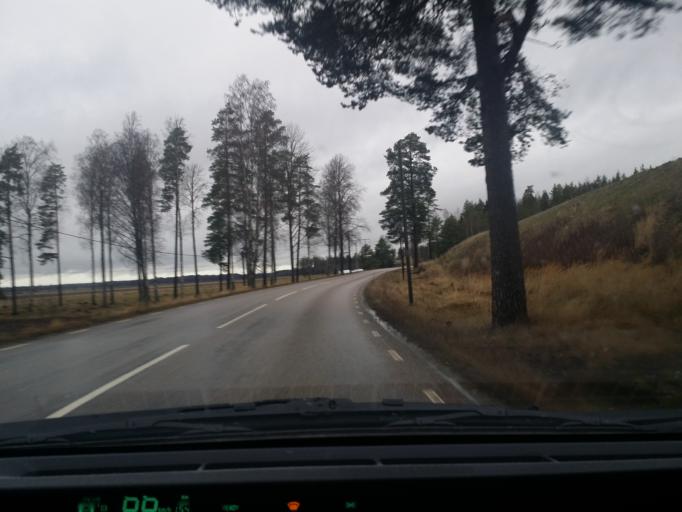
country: SE
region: Vaestmanland
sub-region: Sala Kommun
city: Sala
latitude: 59.8165
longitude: 16.5334
